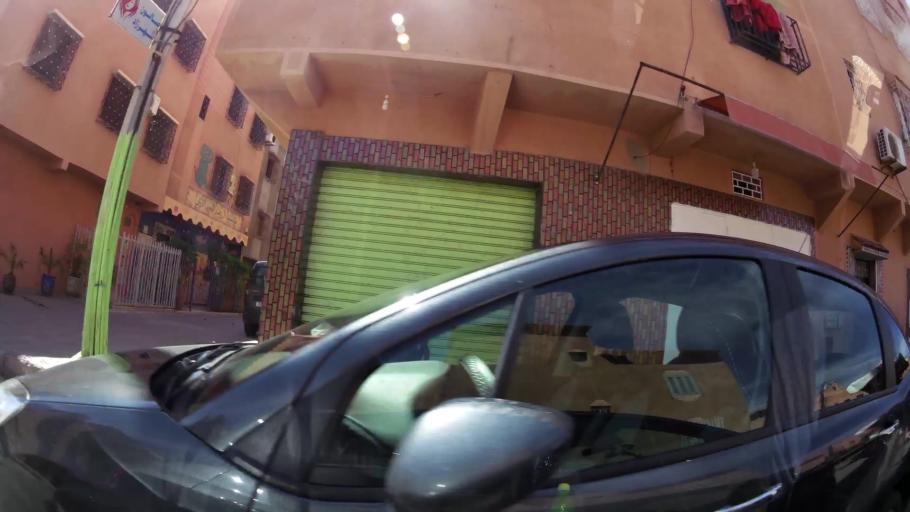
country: MA
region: Marrakech-Tensift-Al Haouz
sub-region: Marrakech
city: Marrakesh
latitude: 31.6456
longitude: -8.0664
